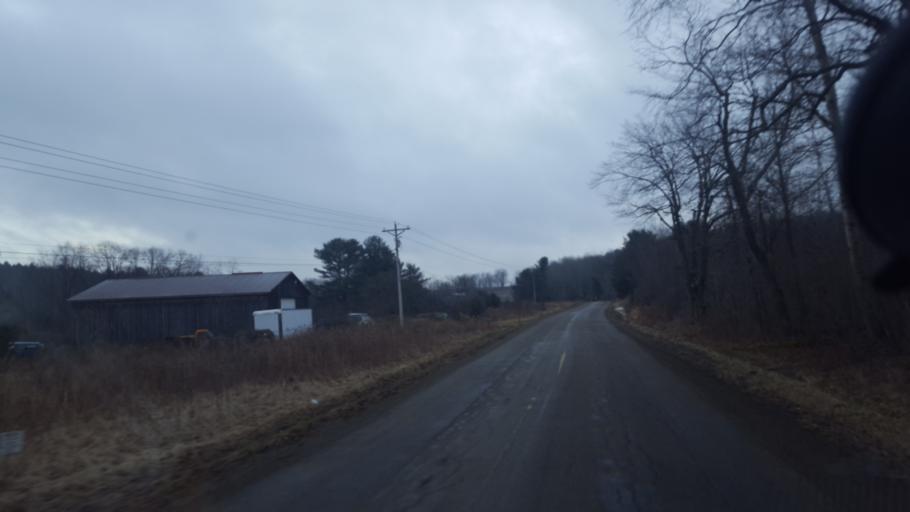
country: US
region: New York
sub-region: Allegany County
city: Andover
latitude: 41.9877
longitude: -77.7526
